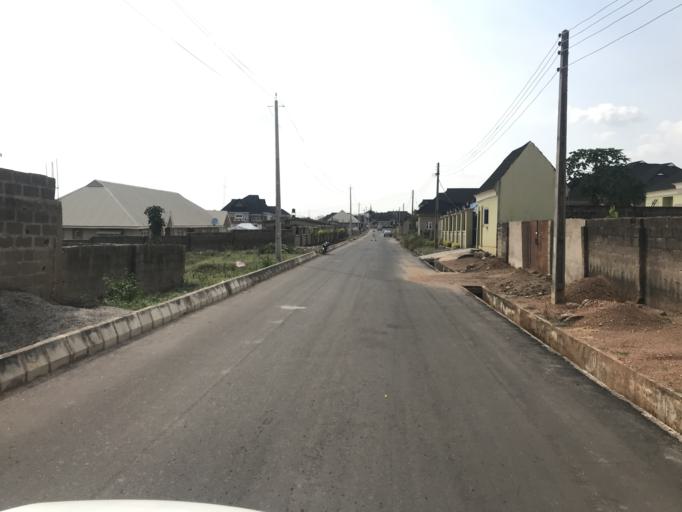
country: NG
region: Osun
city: Osogbo
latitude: 7.8109
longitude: 4.5548
